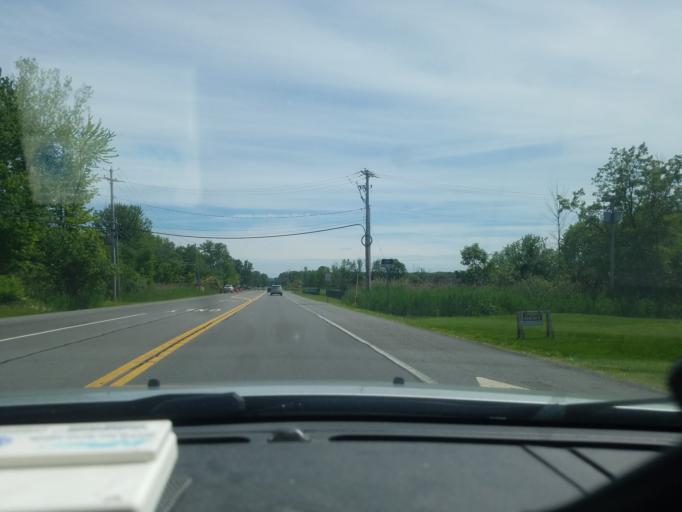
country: US
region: New York
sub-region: Onondaga County
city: East Syracuse
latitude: 43.0830
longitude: -76.0587
